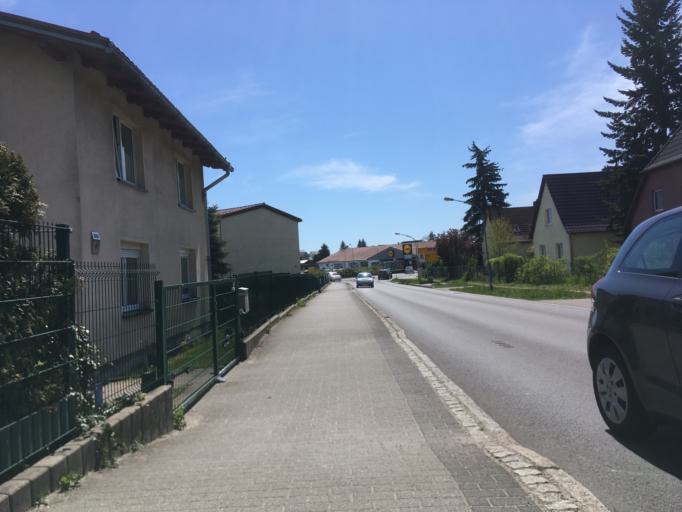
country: DE
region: Brandenburg
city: Wildau
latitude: 52.3241
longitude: 13.6146
